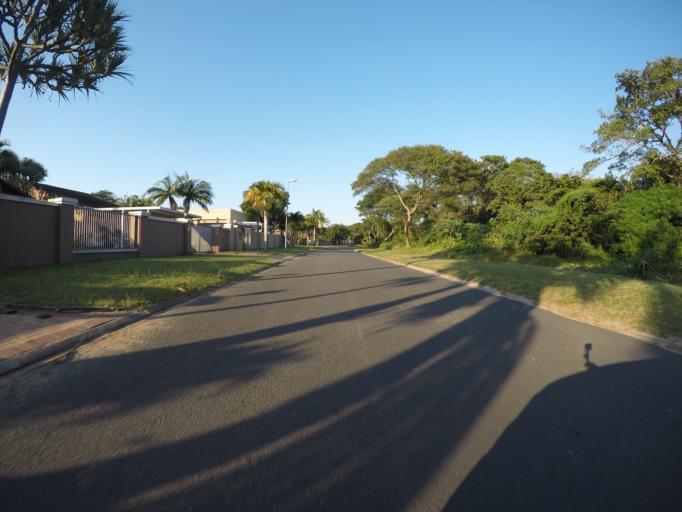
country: ZA
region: KwaZulu-Natal
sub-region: uThungulu District Municipality
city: Richards Bay
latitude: -28.7756
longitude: 32.1169
